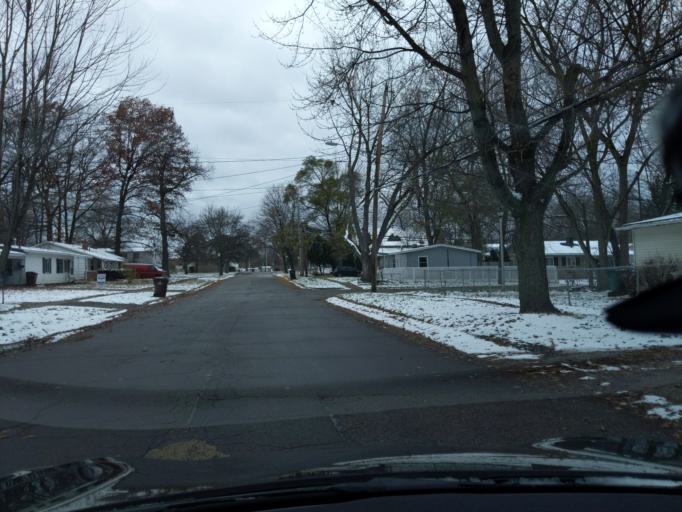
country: US
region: Michigan
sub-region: Ingham County
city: Lansing
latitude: 42.6907
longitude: -84.5912
